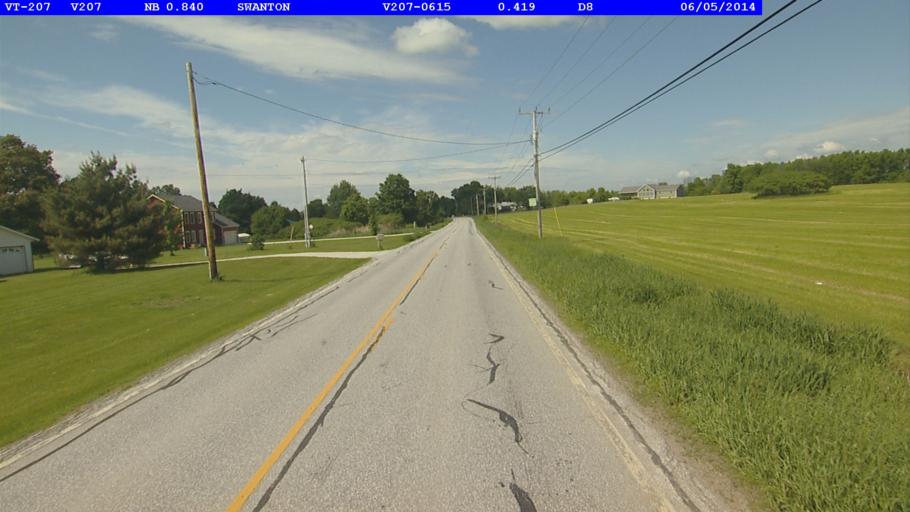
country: US
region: Vermont
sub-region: Franklin County
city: Saint Albans
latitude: 44.8510
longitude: -73.0760
